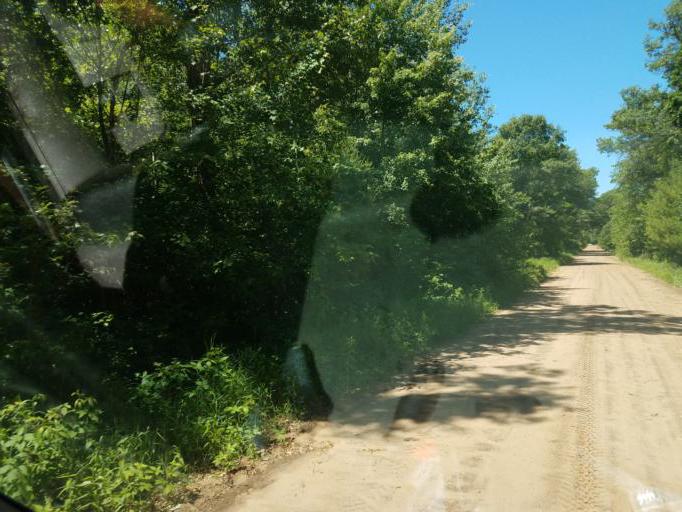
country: US
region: Wisconsin
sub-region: Adams County
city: Friendship
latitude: 44.0248
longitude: -89.9846
